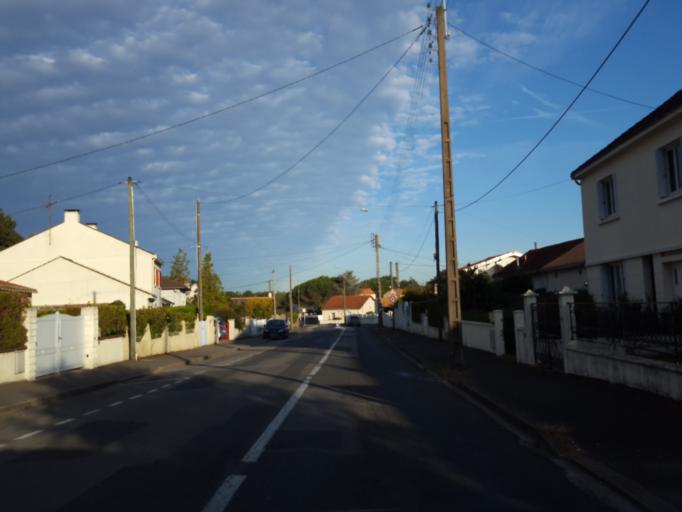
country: FR
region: Pays de la Loire
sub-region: Departement de la Loire-Atlantique
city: Basse-Goulaine
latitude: 47.1934
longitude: -1.4776
